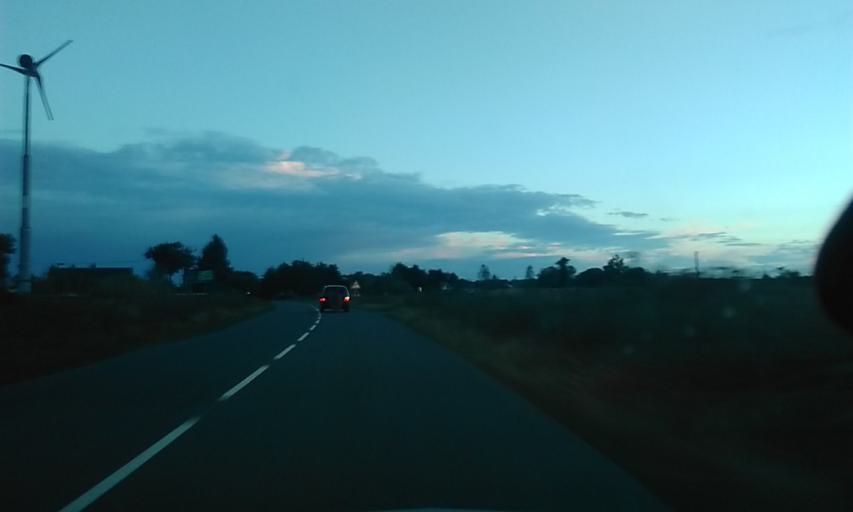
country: FR
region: Brittany
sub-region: Departement d'Ille-et-Vilaine
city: Saint-Thurial
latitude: 48.0433
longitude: -1.9279
